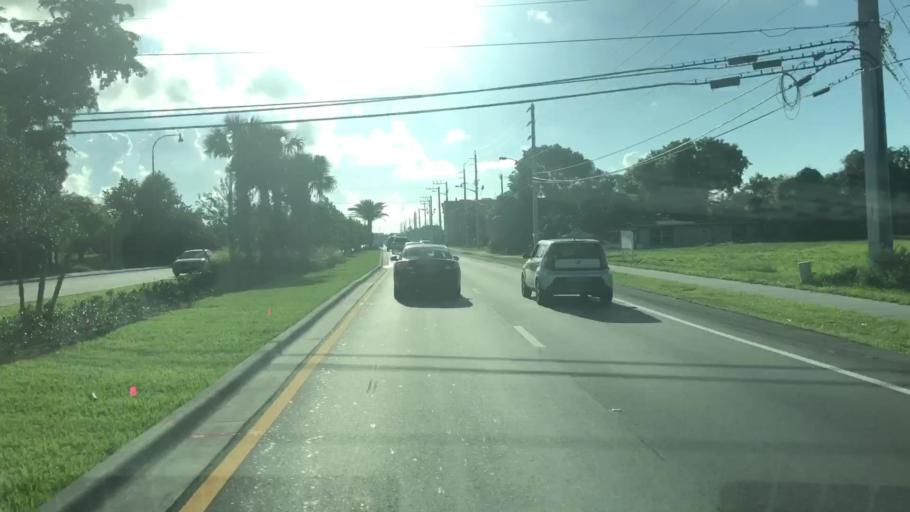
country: US
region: Florida
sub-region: Broward County
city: Coconut Creek
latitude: 26.2452
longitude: -80.1638
